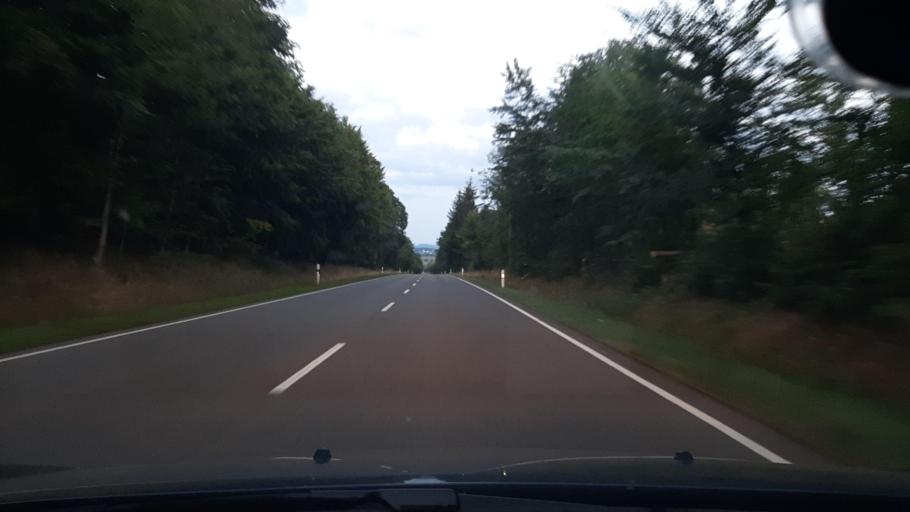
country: DE
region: North Rhine-Westphalia
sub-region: Regierungsbezirk Koln
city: Dahlem
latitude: 50.4490
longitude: 6.5732
